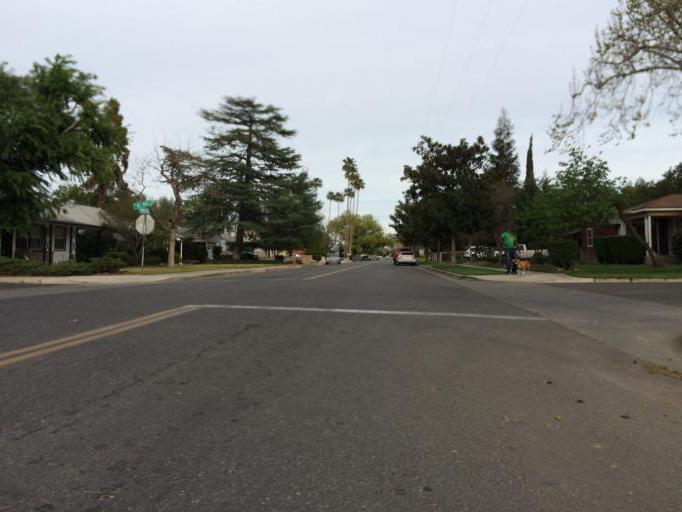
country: US
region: California
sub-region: Fresno County
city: Fresno
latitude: 36.7759
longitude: -119.7953
